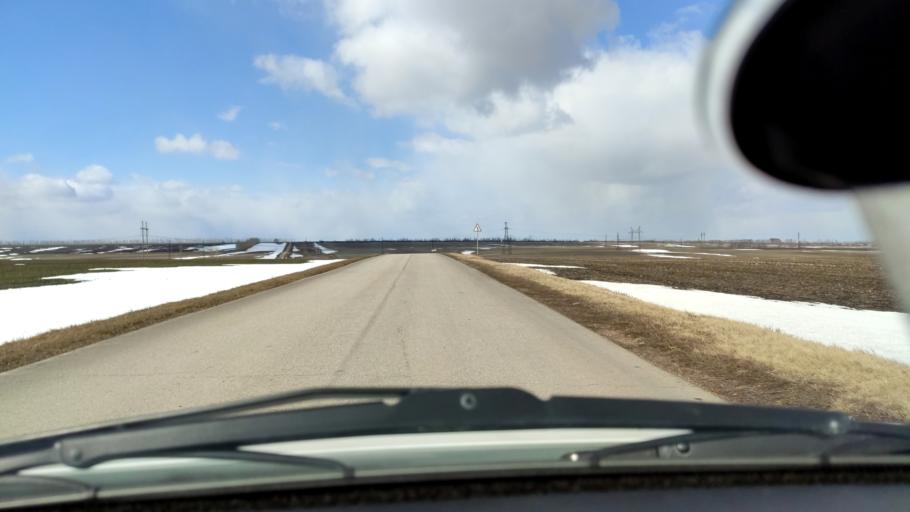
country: RU
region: Bashkortostan
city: Tolbazy
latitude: 54.1707
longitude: 55.9307
